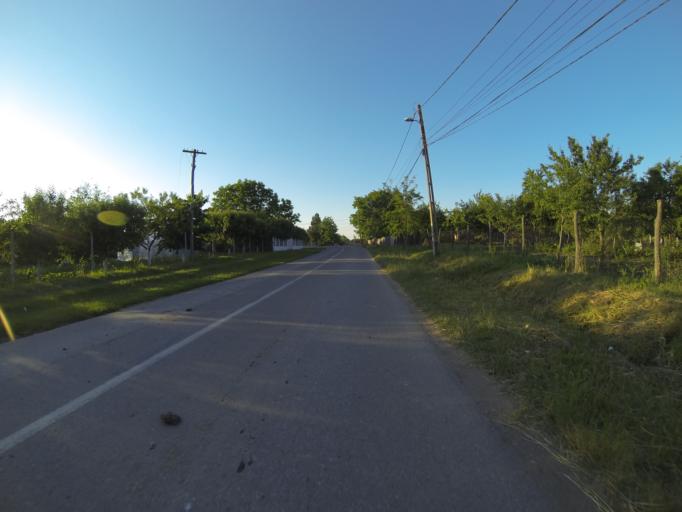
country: RO
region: Dolj
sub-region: Comuna Caloparu
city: Calopar
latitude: 44.1631
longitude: 23.7636
